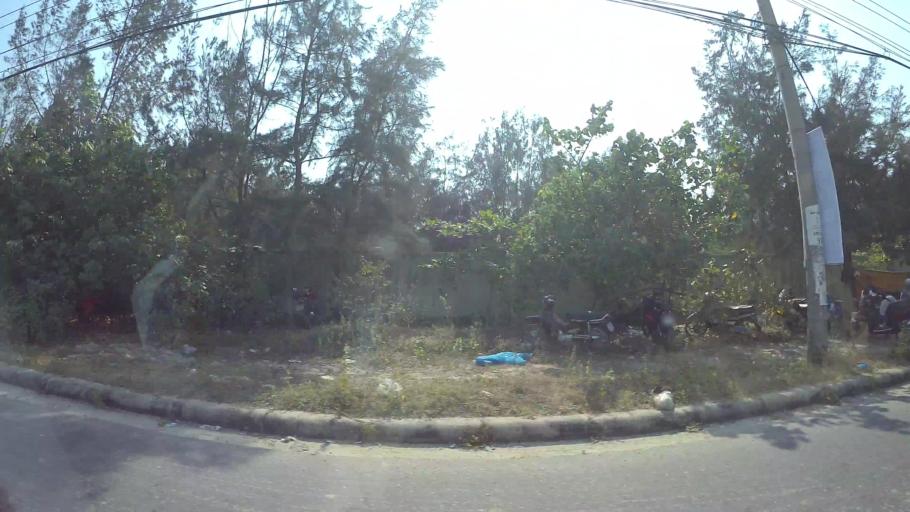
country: VN
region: Da Nang
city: Ngu Hanh Son
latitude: 15.9720
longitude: 108.2813
